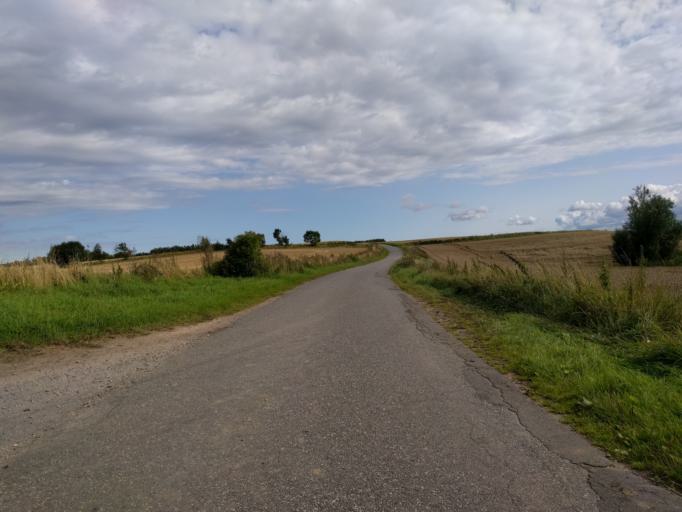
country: DK
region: South Denmark
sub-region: Kerteminde Kommune
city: Kerteminde
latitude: 55.4639
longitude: 10.6201
